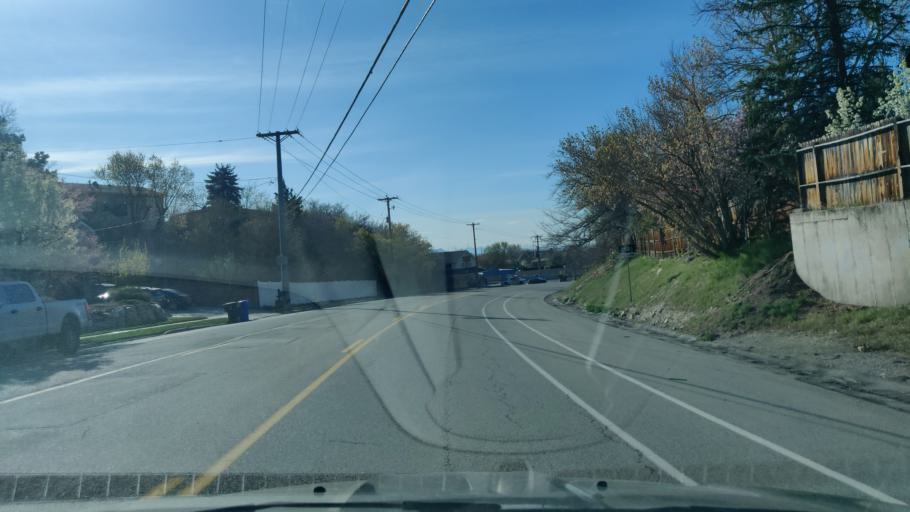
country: US
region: Utah
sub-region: Salt Lake County
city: Cottonwood Heights
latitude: 40.6096
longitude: -111.8164
